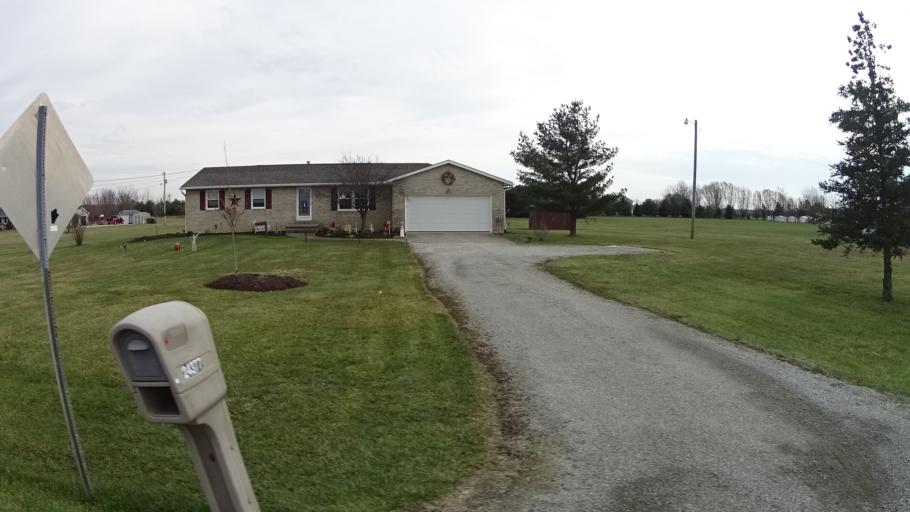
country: US
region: Ohio
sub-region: Lorain County
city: Wellington
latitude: 41.1390
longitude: -82.1698
